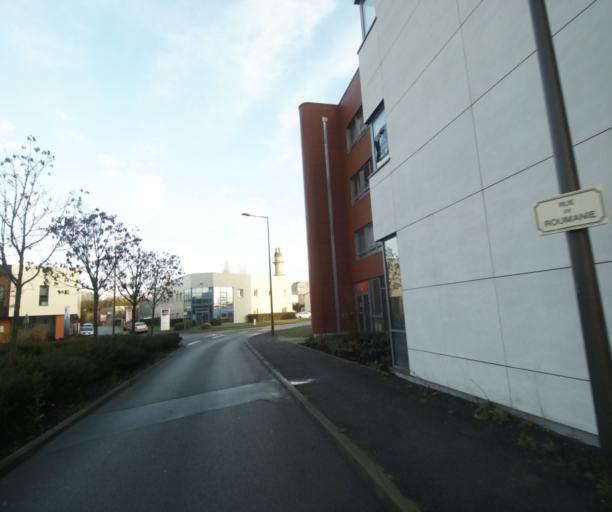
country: FR
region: Pays de la Loire
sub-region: Departement de la Sarthe
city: Le Mans
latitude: 47.9957
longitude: 0.2338
